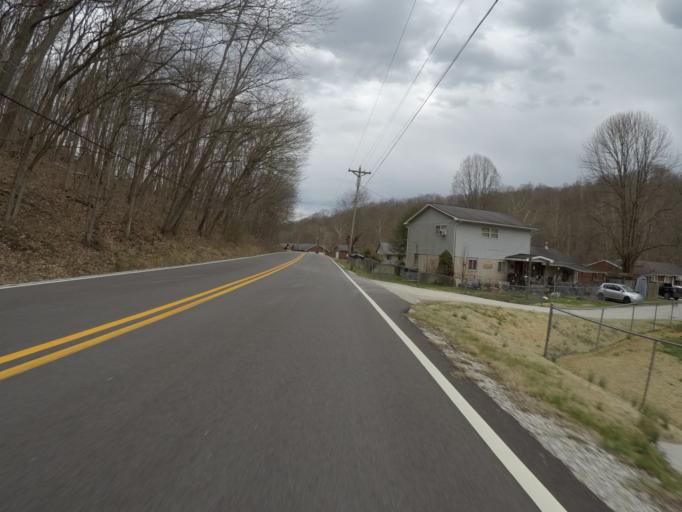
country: US
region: Ohio
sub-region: Lawrence County
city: Burlington
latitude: 38.4506
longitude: -82.5169
